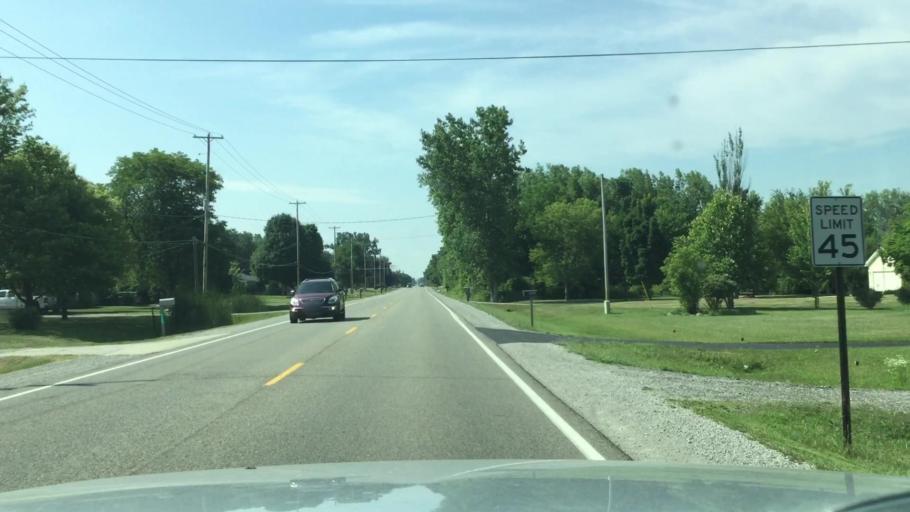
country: US
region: Michigan
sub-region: Genesee County
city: Flushing
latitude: 43.0743
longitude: -83.8134
